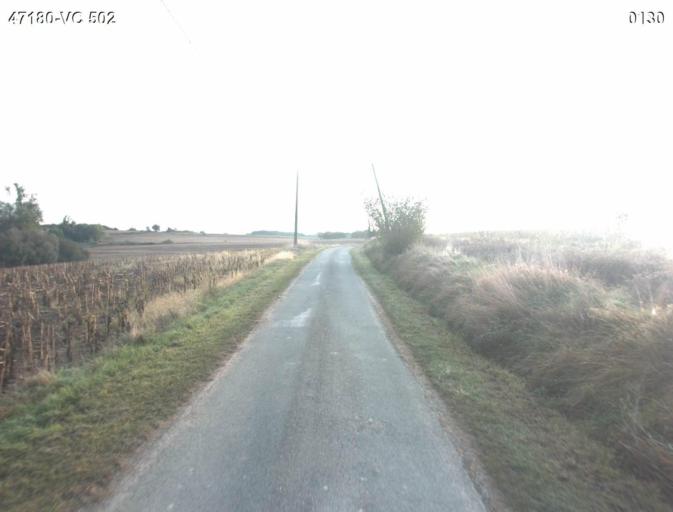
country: FR
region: Aquitaine
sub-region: Departement du Lot-et-Garonne
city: Sainte-Colombe-en-Bruilhois
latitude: 44.1621
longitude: 0.4762
